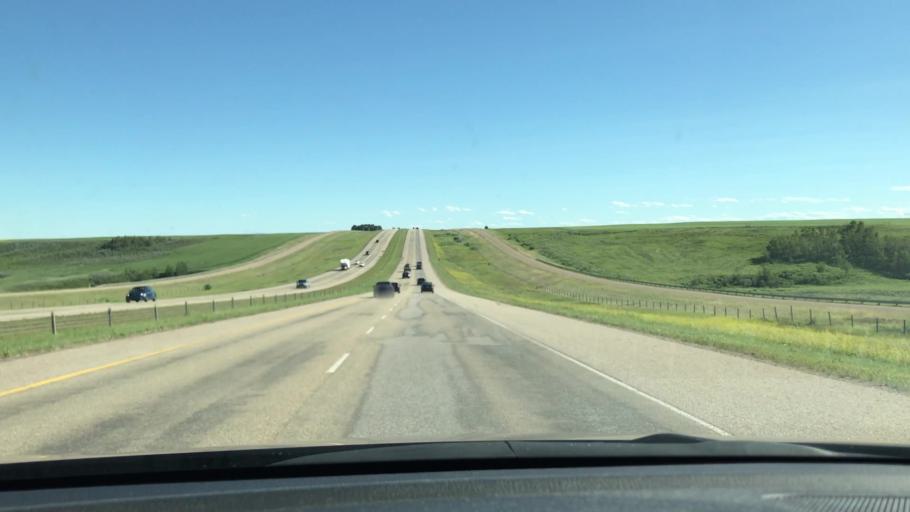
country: CA
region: Alberta
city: Carstairs
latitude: 51.6011
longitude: -114.0254
